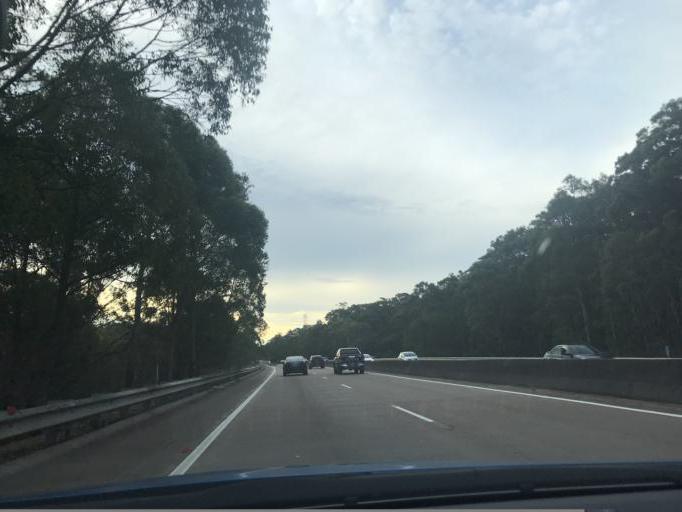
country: AU
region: New South Wales
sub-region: Lake Macquarie Shire
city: Glendale
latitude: -32.9072
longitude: 151.6393
